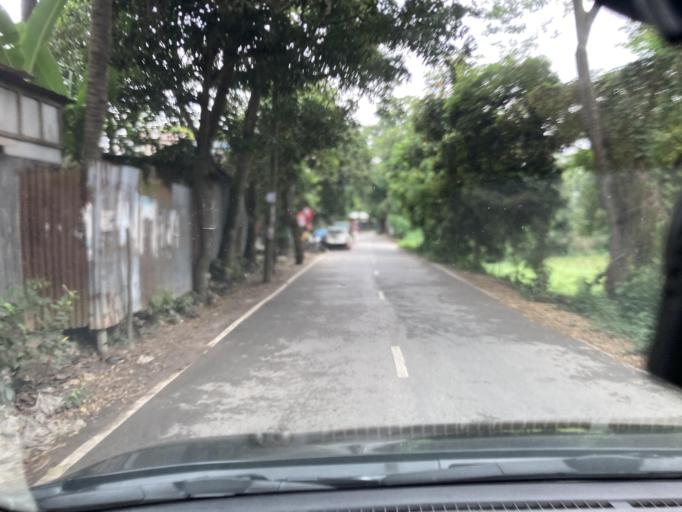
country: BD
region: Dhaka
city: Azimpur
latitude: 23.7833
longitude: 90.2124
